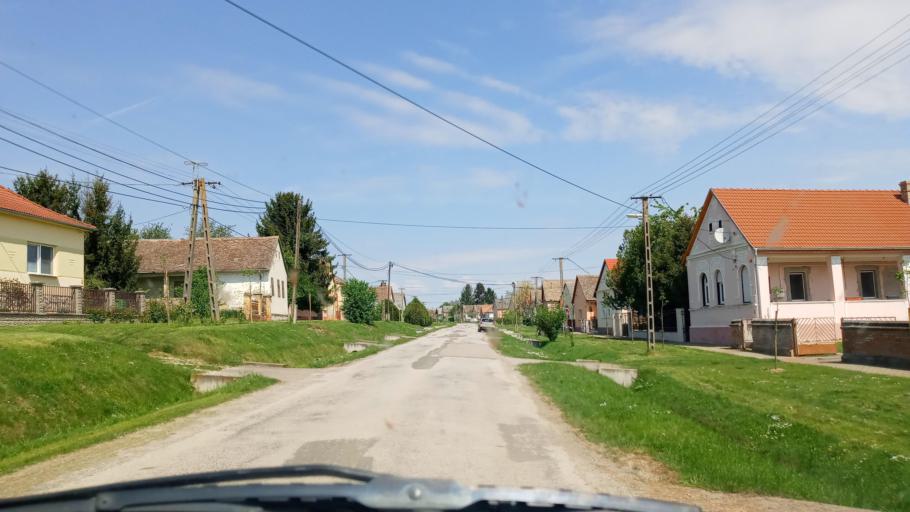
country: HR
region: Osjecko-Baranjska
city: Beli Manastir
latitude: 45.8650
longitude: 18.5858
